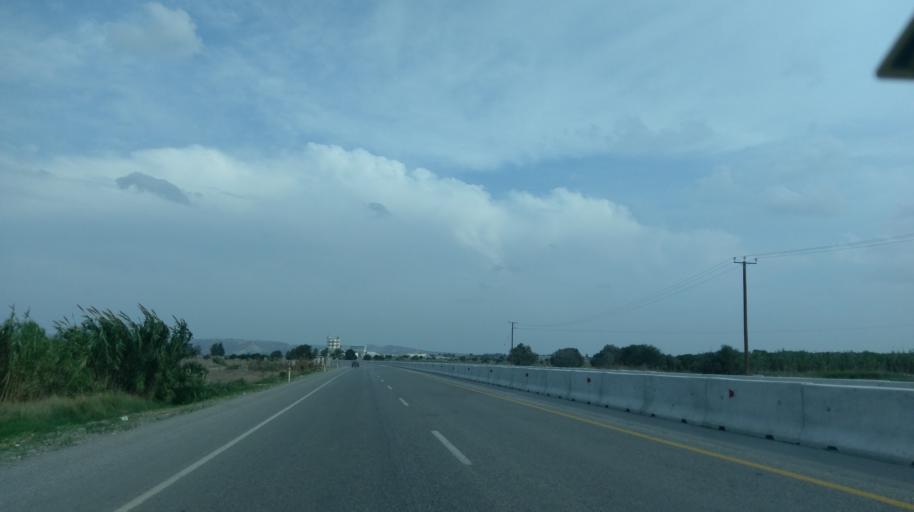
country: CY
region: Lefkosia
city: Morfou
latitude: 35.2007
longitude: 33.0318
